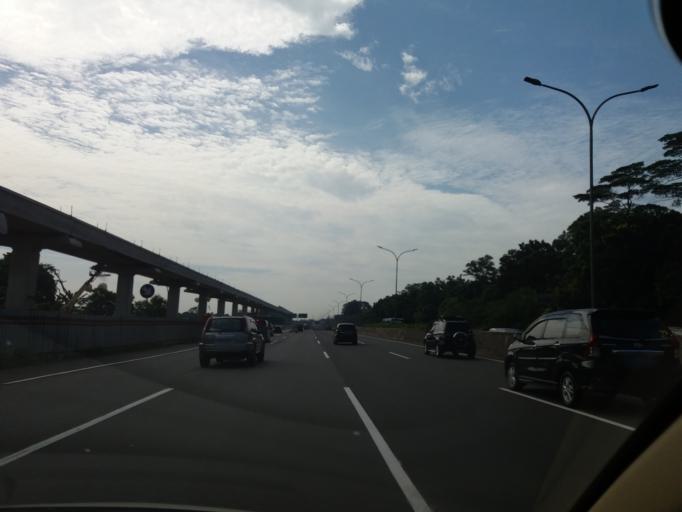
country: ID
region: West Java
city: Cileungsir
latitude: -6.3267
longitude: 106.8870
